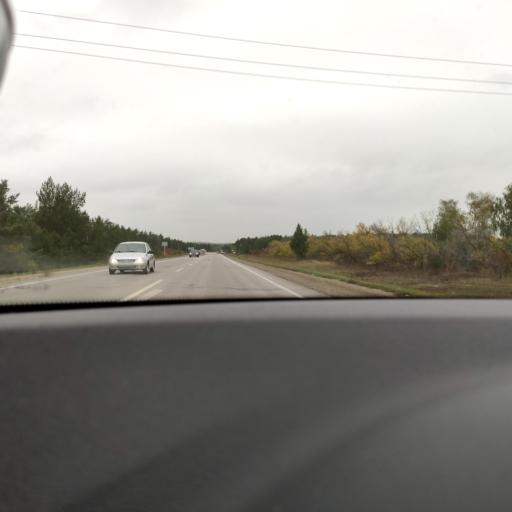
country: RU
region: Samara
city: Mirnyy
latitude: 53.5255
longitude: 50.3148
